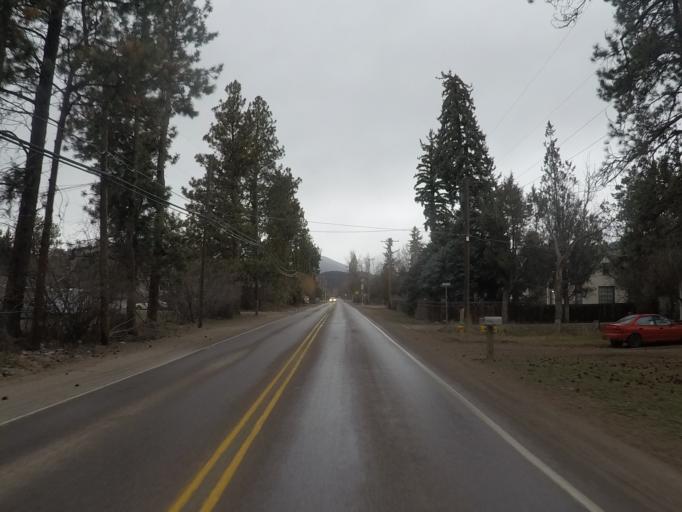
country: US
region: Montana
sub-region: Missoula County
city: East Missoula
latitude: 46.8890
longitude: -113.9657
